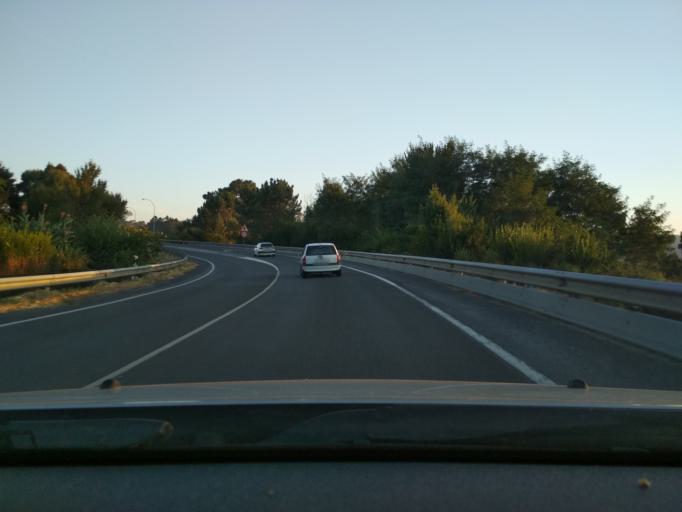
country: ES
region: Galicia
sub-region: Provincia da Coruna
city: Culleredo
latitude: 43.2842
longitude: -8.3674
